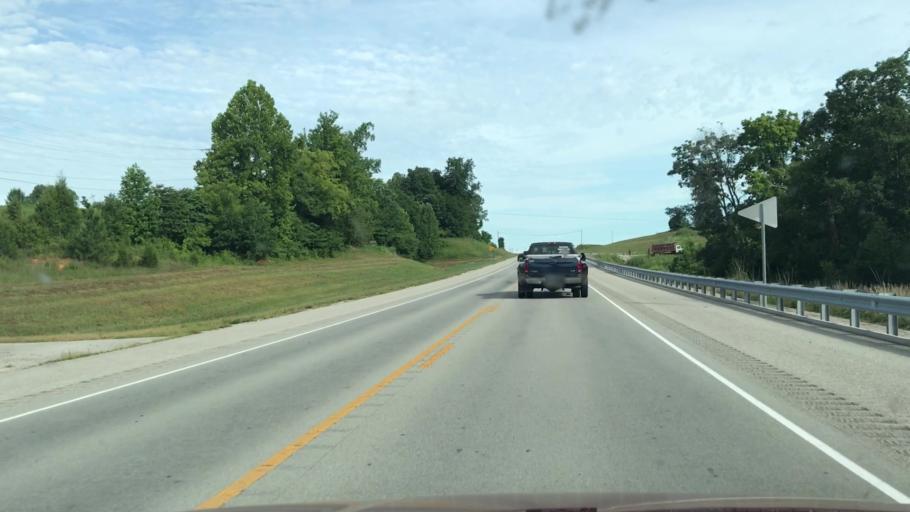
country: US
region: Kentucky
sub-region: Edmonson County
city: Brownsville
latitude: 37.1626
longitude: -86.2242
